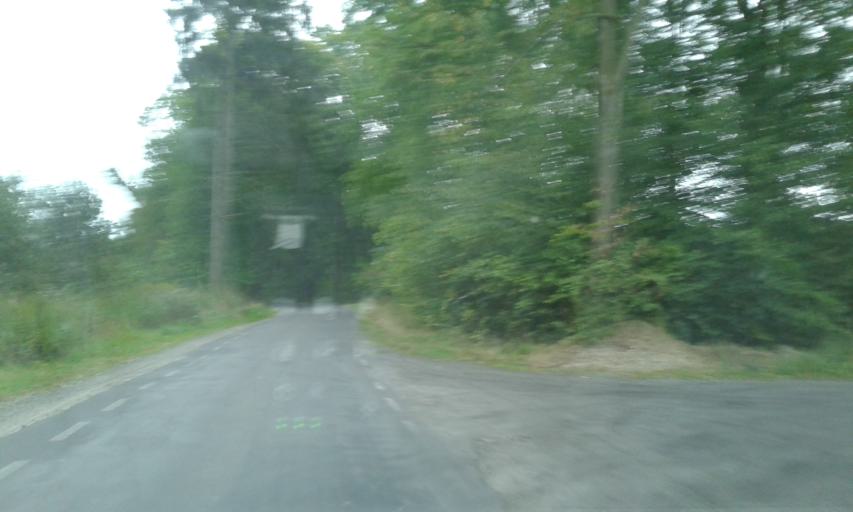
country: PL
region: West Pomeranian Voivodeship
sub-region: Powiat stargardzki
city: Dolice
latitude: 53.1734
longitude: 15.2562
